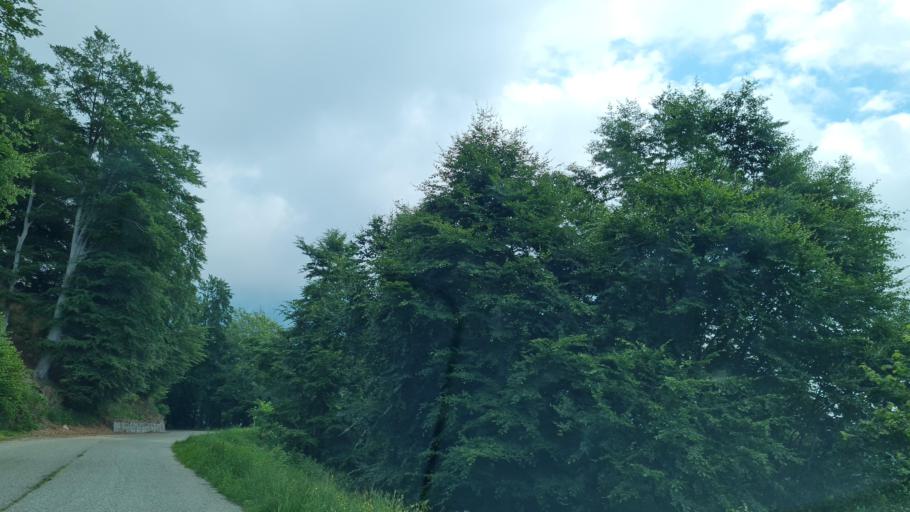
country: IT
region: Piedmont
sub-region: Provincia di Biella
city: Sordevolo
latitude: 45.6131
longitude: 7.9818
